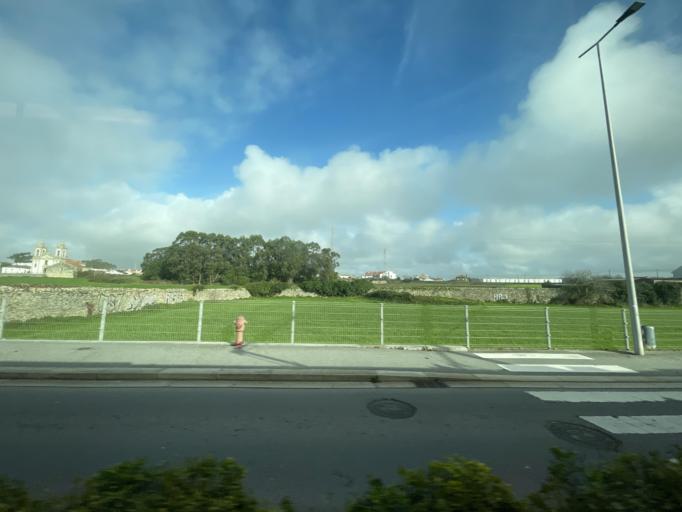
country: PT
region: Porto
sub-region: Vila do Conde
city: Vila do Conde
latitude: 41.3575
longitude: -8.7384
